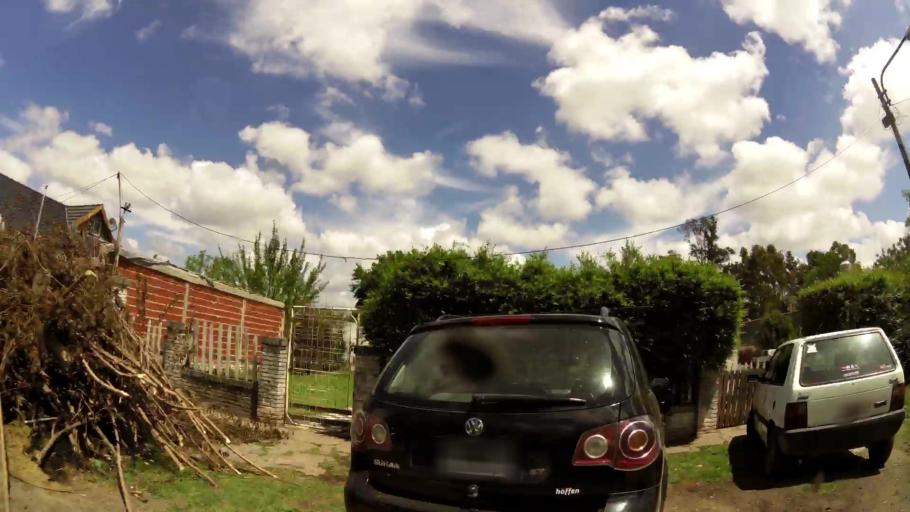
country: AR
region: Buenos Aires
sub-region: Partido de Quilmes
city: Quilmes
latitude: -34.8112
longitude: -58.2339
